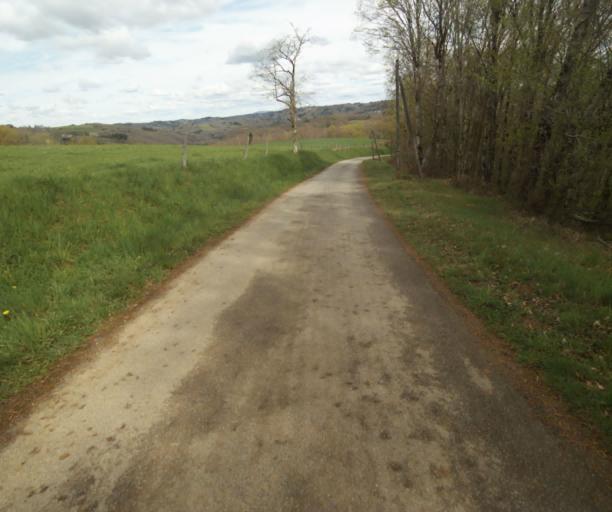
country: FR
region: Limousin
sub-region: Departement de la Correze
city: Laguenne
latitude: 45.2275
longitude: 1.8488
